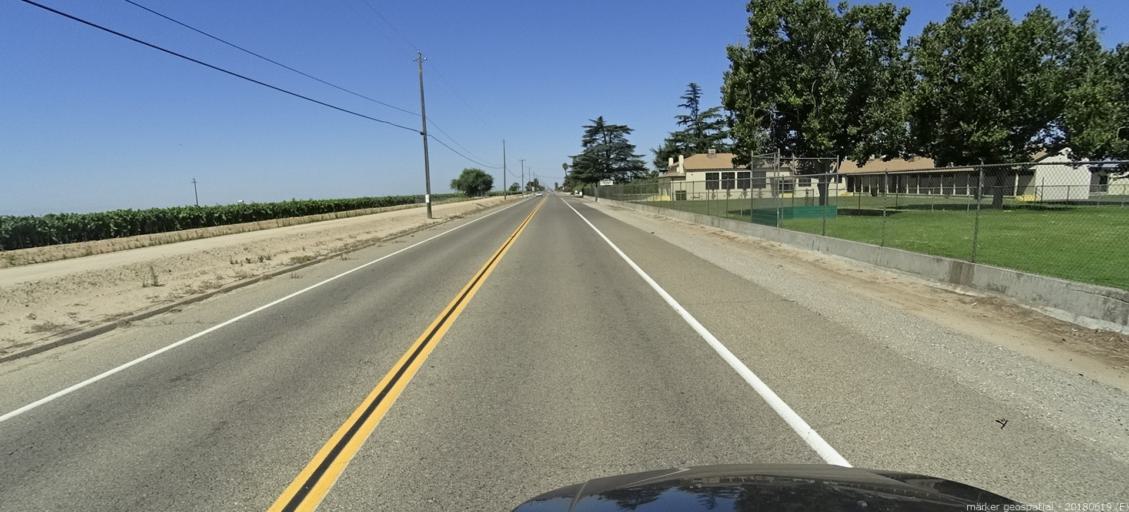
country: US
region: California
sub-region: Fresno County
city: Biola
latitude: 36.8513
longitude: -120.0721
